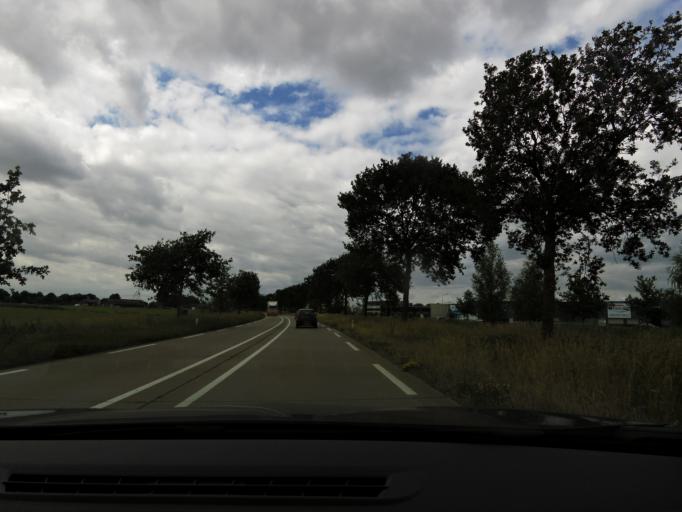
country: NL
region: North Brabant
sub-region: Gemeente Made en Drimmelen
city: Made
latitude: 51.6693
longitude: 4.8276
